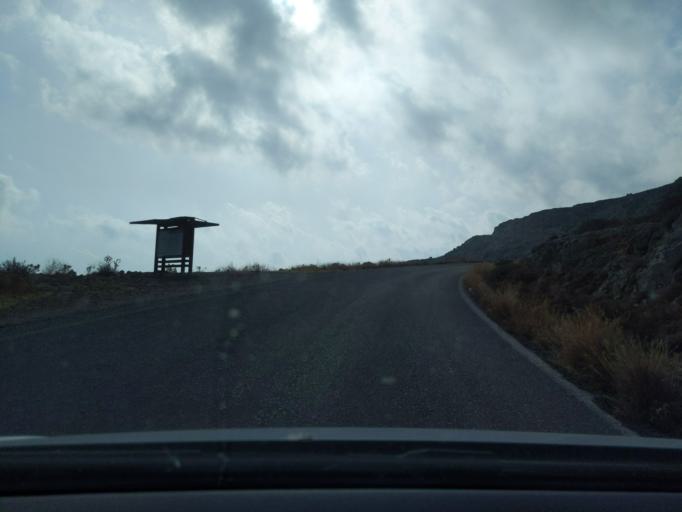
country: GR
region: Crete
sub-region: Nomos Lasithiou
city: Palekastro
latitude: 35.0933
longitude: 26.2629
